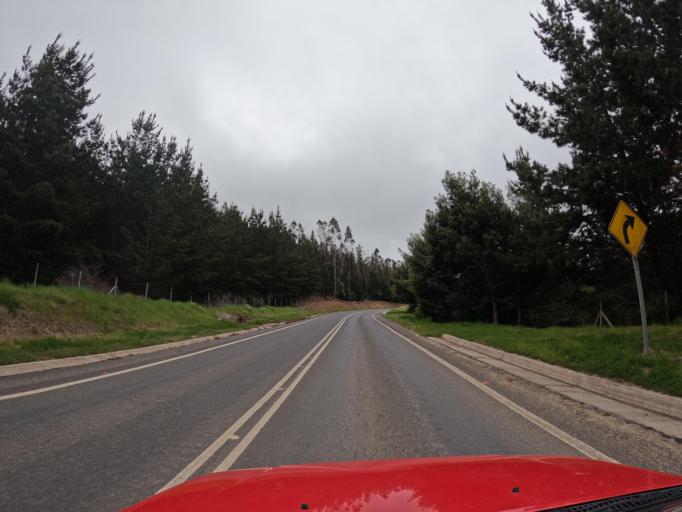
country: CL
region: O'Higgins
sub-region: Provincia de Colchagua
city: Santa Cruz
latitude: -34.5510
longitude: -72.0220
